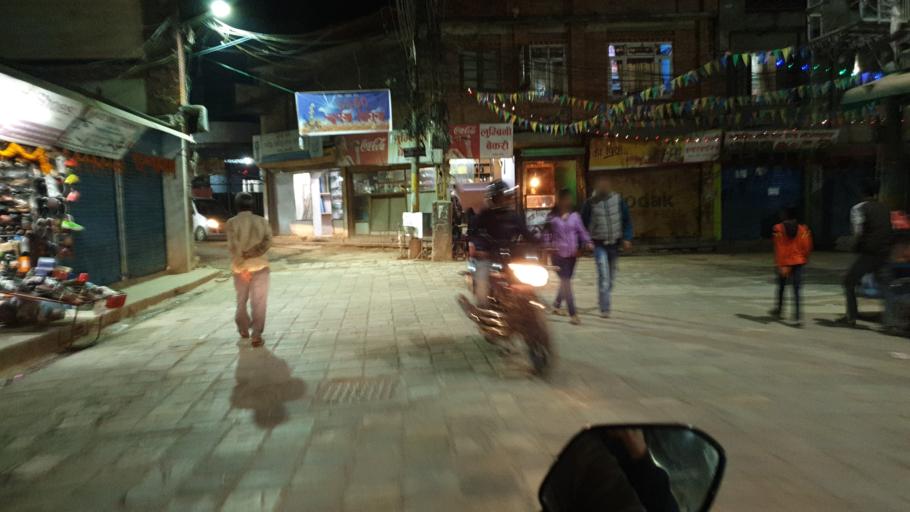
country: NP
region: Central Region
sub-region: Bagmati Zone
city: Kathmandu
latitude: 27.7010
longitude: 85.3077
